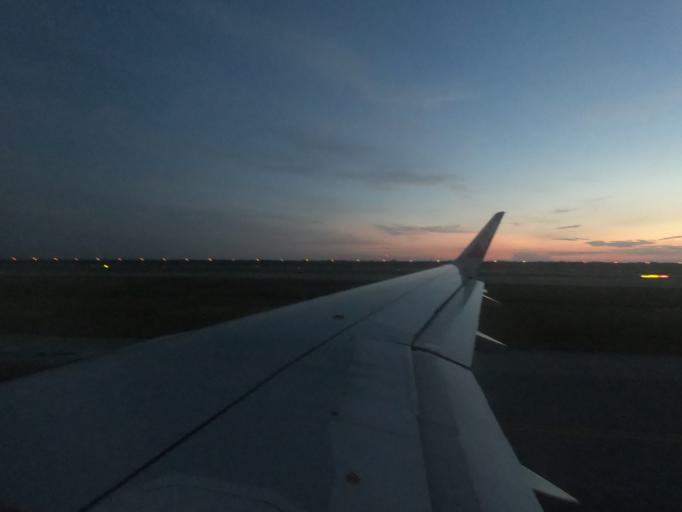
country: MY
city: Sungai Pelek New Village
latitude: 2.7267
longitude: 101.6885
